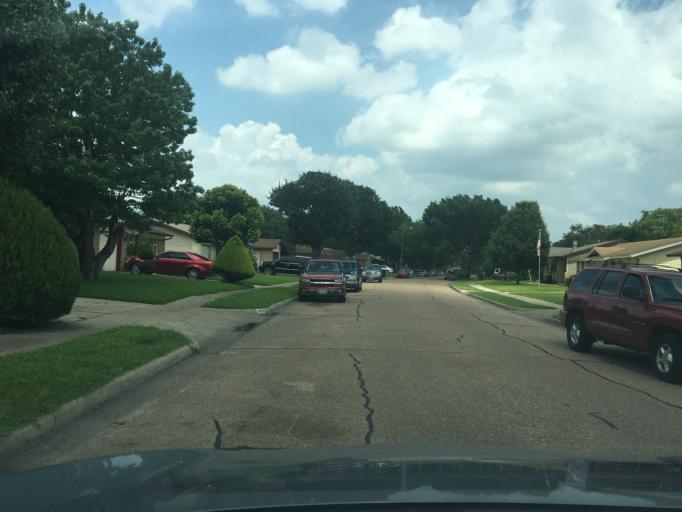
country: US
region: Texas
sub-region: Dallas County
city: Richardson
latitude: 32.9150
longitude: -96.6949
